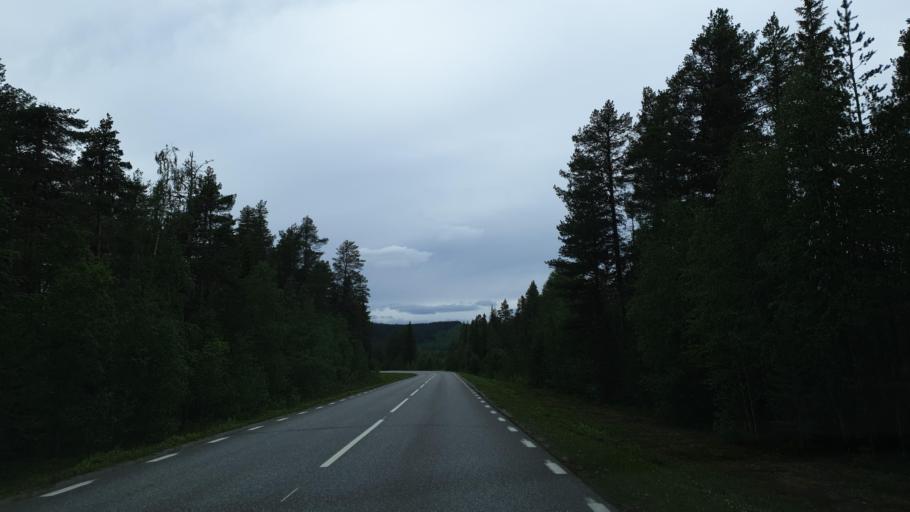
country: SE
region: Vaesterbotten
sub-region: Sorsele Kommun
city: Sorsele
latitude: 65.5512
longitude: 17.4989
